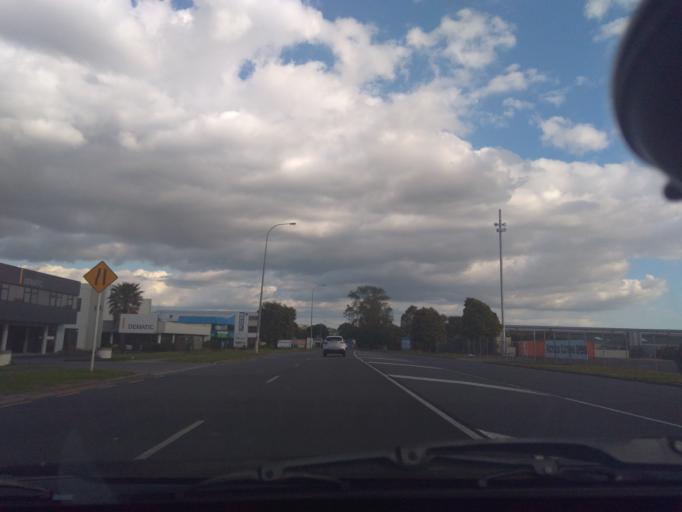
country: NZ
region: Auckland
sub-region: Auckland
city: Manukau City
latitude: -36.9393
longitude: 174.8858
